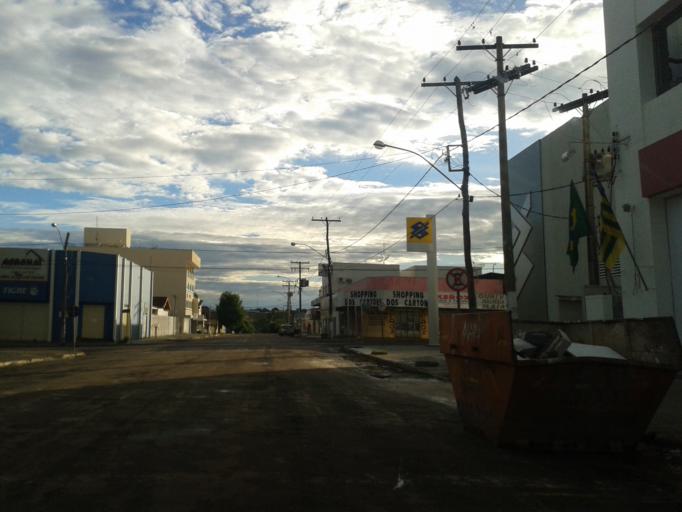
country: BR
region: Goias
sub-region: Sao Miguel Do Araguaia
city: Sao Miguel do Araguaia
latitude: -13.2732
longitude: -50.1625
